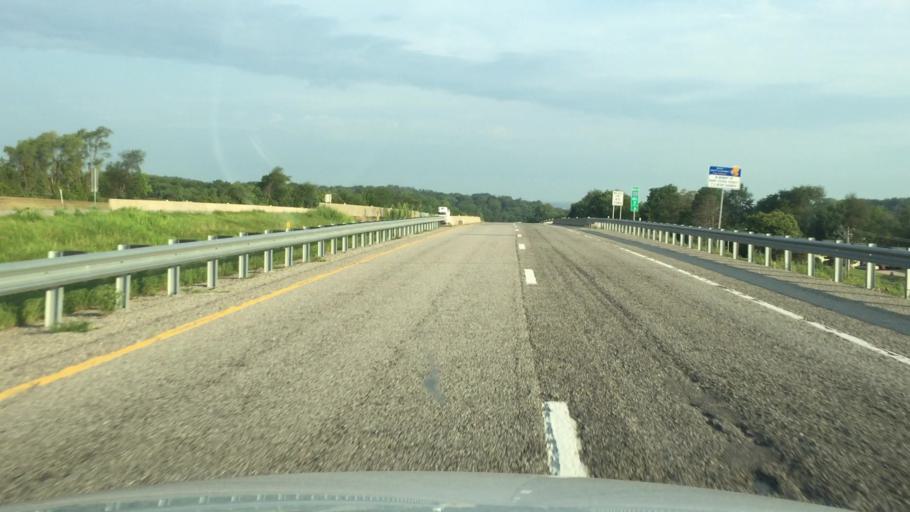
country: US
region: Missouri
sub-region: Buchanan County
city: Saint Joseph
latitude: 39.7214
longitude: -94.8330
